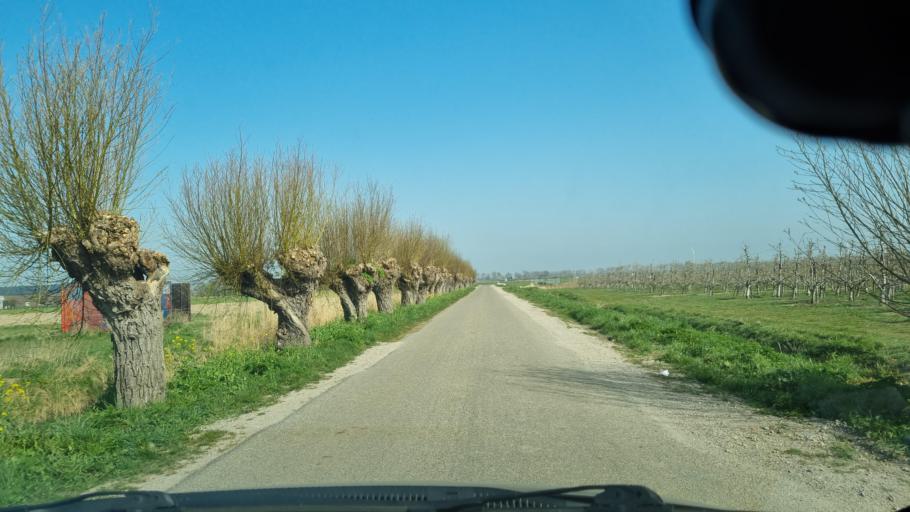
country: NL
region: Gelderland
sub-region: Gemeente Maasdriel
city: Hedel
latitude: 51.7526
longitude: 5.2342
